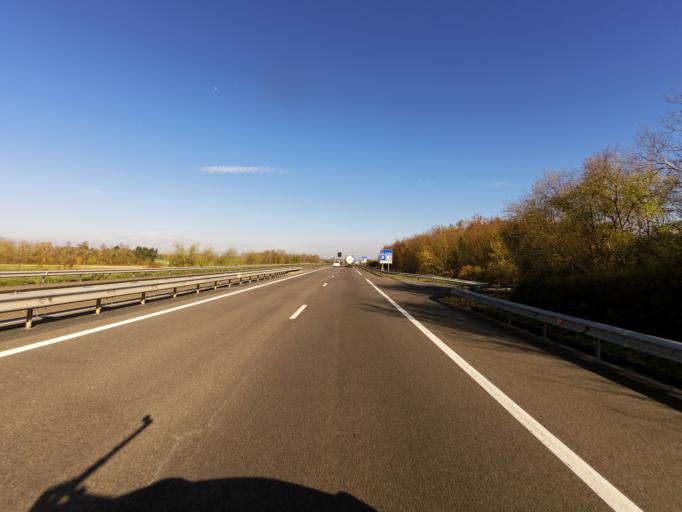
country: FR
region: Champagne-Ardenne
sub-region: Departement de la Marne
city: Fagnieres
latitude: 48.9985
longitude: 4.2975
